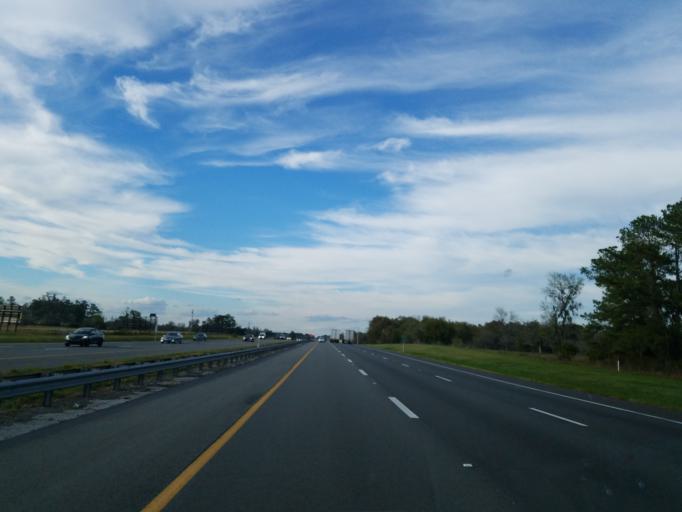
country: US
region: Florida
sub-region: Marion County
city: Citra
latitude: 29.3130
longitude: -82.2091
